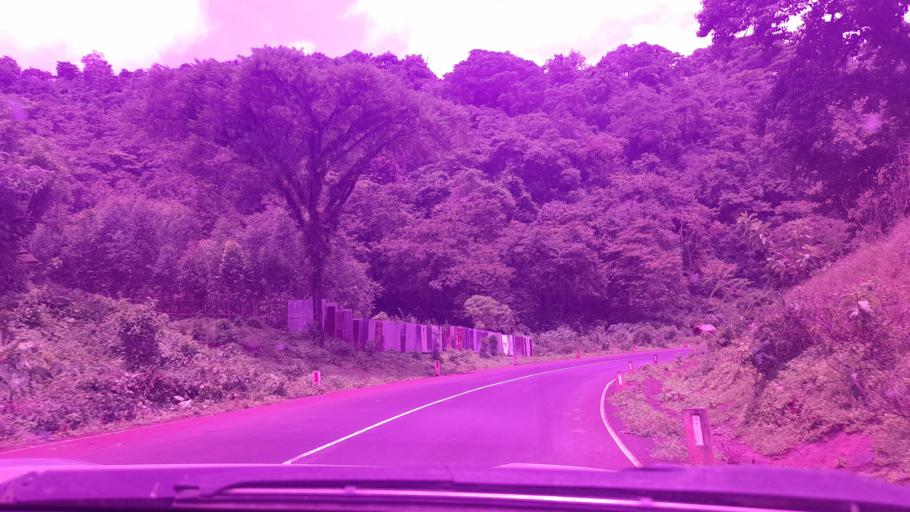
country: ET
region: Oromiya
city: Metu
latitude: 8.3328
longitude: 35.7470
